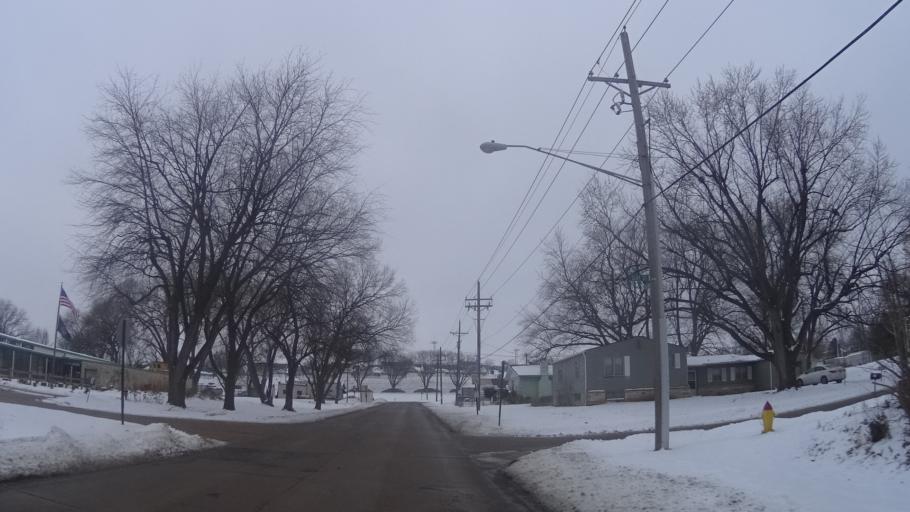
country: US
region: Nebraska
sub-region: Sarpy County
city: Bellevue
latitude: 41.1345
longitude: -95.9052
